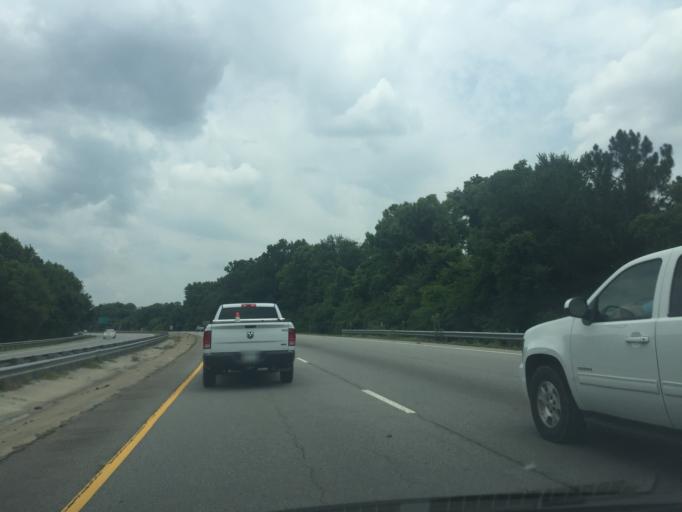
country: US
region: Georgia
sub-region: Chatham County
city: Thunderbolt
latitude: 32.0490
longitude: -81.0687
